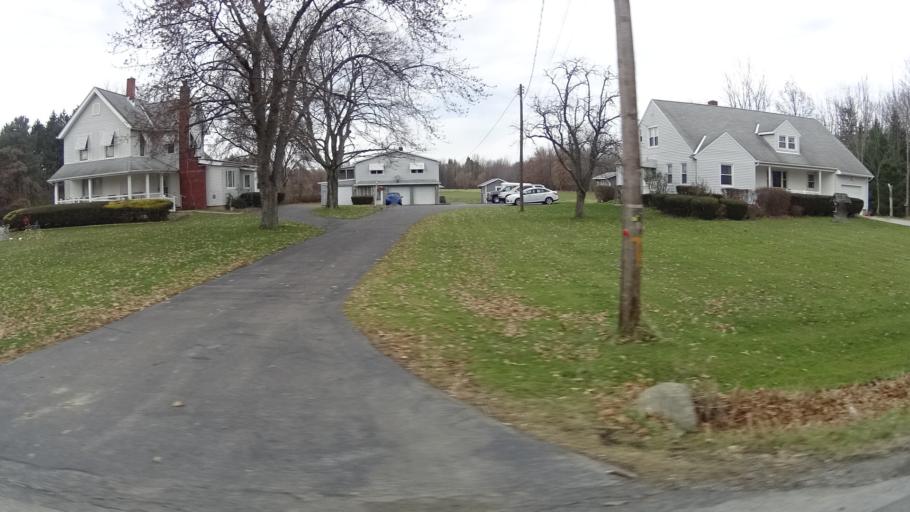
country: US
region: Ohio
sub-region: Cuyahoga County
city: Strongsville
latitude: 41.3126
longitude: -81.8926
